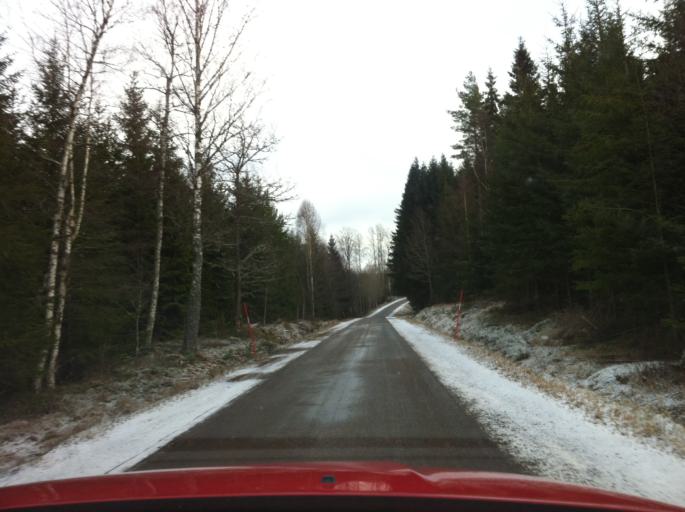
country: SE
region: Joenkoeping
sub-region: Eksjo Kommun
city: Mariannelund
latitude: 57.6131
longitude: 15.6785
